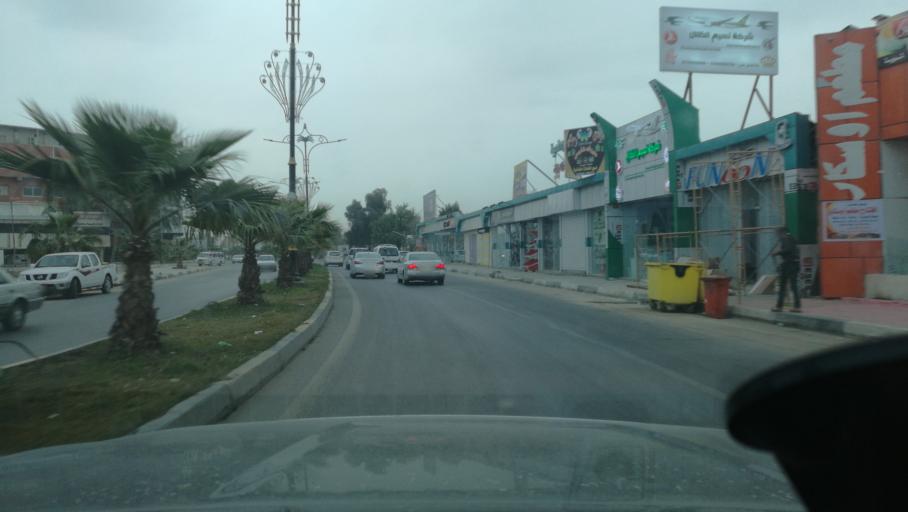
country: IQ
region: Basra Governorate
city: Al Basrah al Qadimah
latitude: 30.4990
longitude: 47.8365
